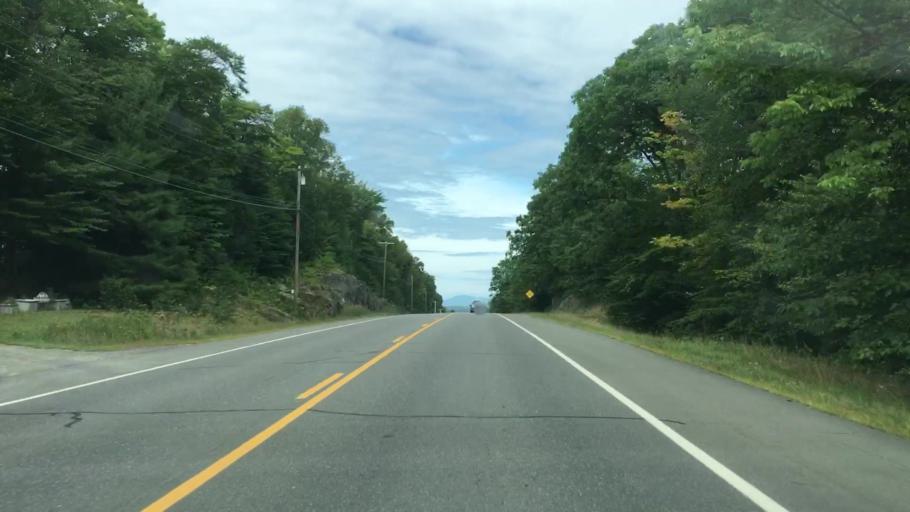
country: US
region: Maine
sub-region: Piscataquis County
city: Brownville
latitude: 45.2842
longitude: -69.0127
